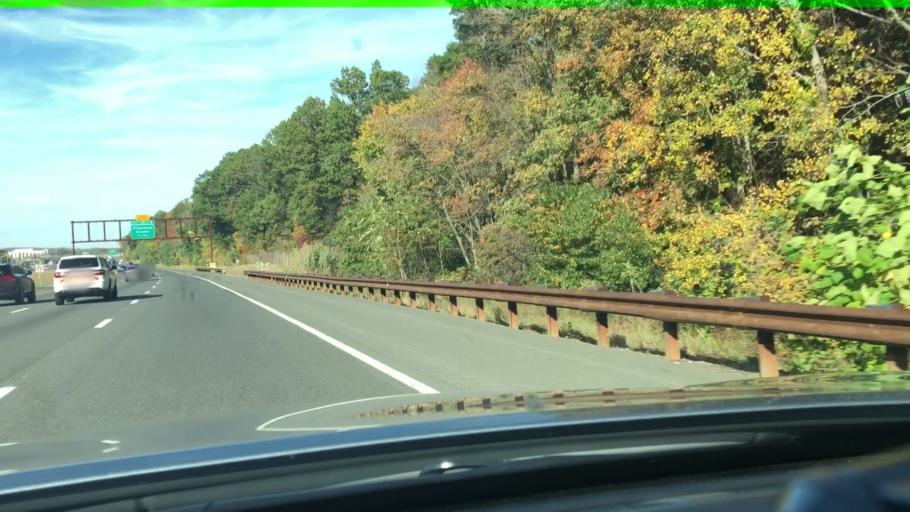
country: US
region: New Jersey
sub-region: Bergen County
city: Paramus
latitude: 40.9509
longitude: -74.0658
